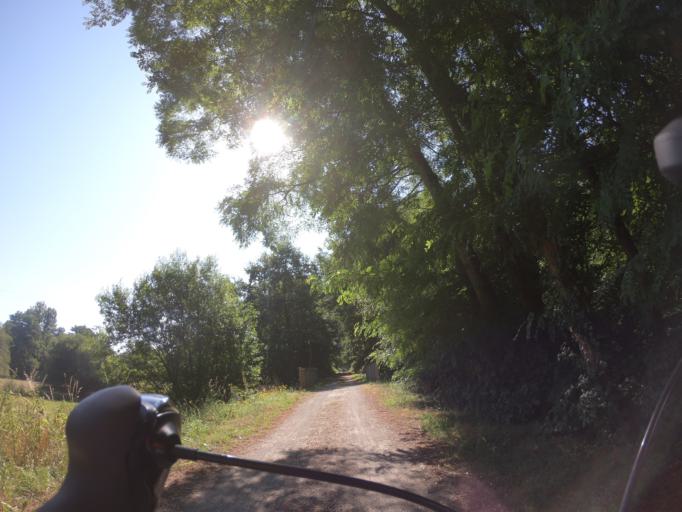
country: FR
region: Lower Normandy
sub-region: Departement de la Manche
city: Barenton
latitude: 48.5914
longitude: -0.8558
